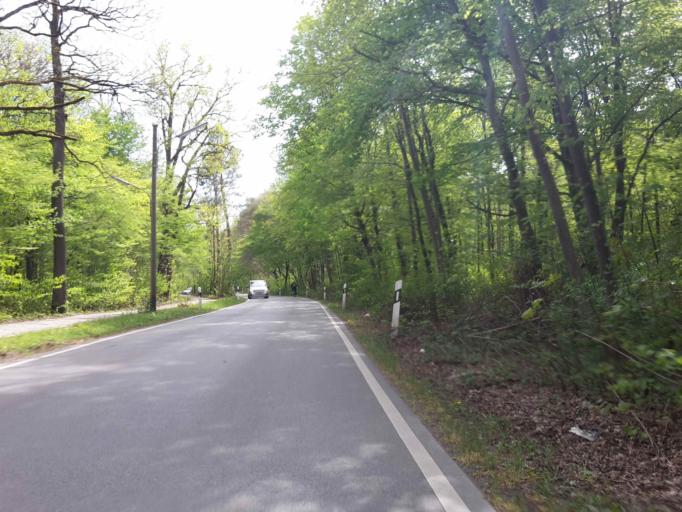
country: DE
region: Bavaria
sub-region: Upper Bavaria
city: Pasing
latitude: 48.1688
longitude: 11.4934
